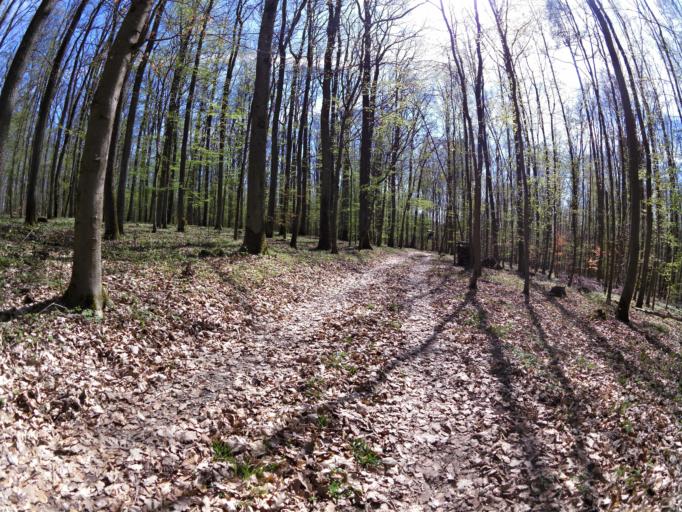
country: DE
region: Bavaria
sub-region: Regierungsbezirk Unterfranken
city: Hettstadt
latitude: 49.8082
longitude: 9.7996
